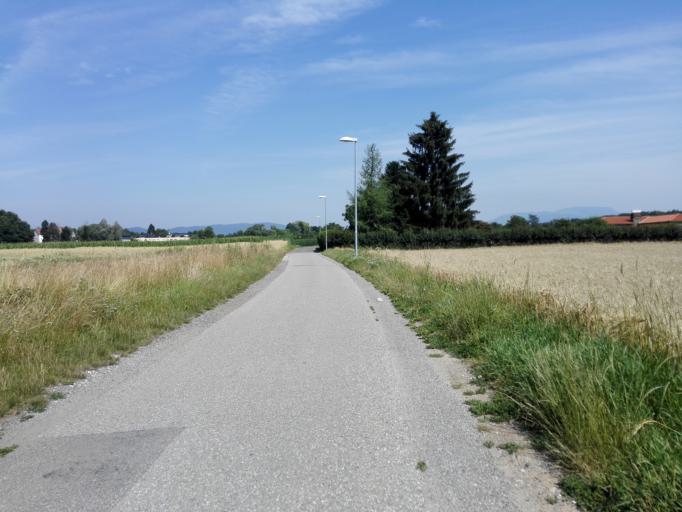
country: AT
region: Styria
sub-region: Politischer Bezirk Graz-Umgebung
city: Feldkirchen bei Graz
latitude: 47.0010
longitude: 15.4560
